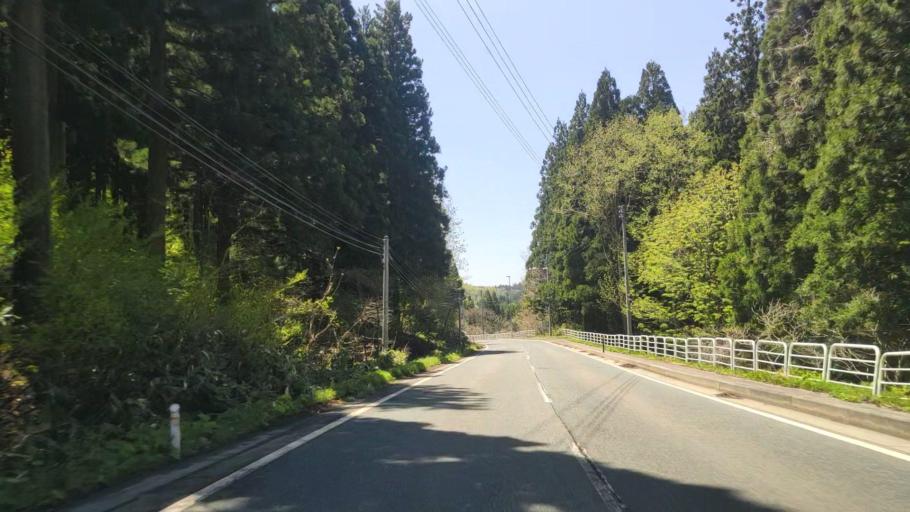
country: JP
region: Yamagata
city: Shinjo
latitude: 38.8966
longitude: 140.3269
